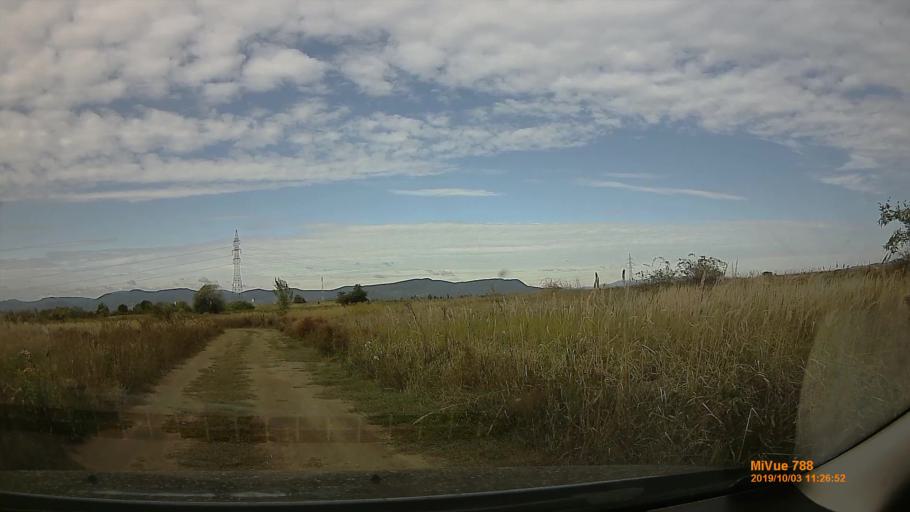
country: HU
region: Pest
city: Dunakeszi
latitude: 47.6534
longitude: 19.1677
